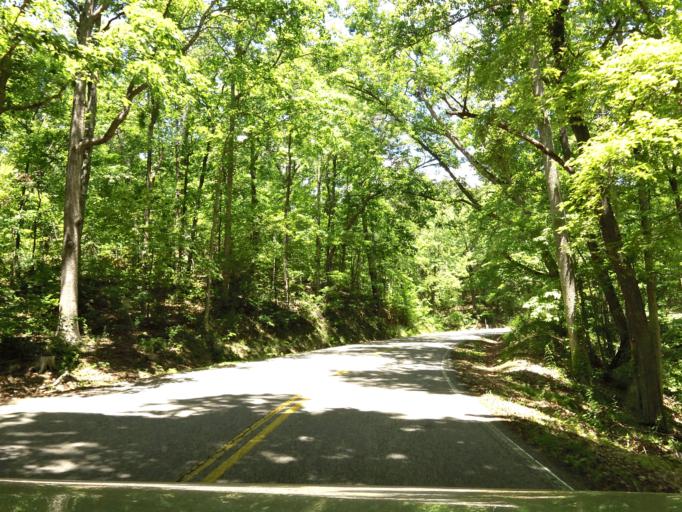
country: US
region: North Carolina
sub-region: Graham County
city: Robbinsville
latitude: 35.5037
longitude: -83.9679
